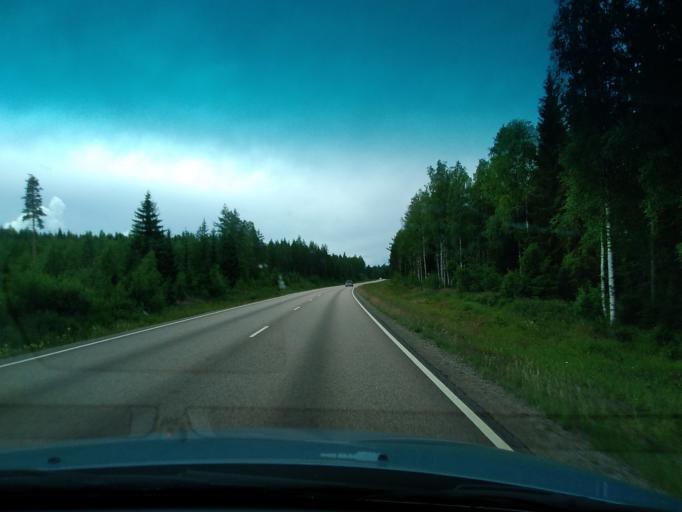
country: FI
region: Central Finland
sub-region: Keuruu
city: Multia
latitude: 62.3821
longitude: 24.7516
